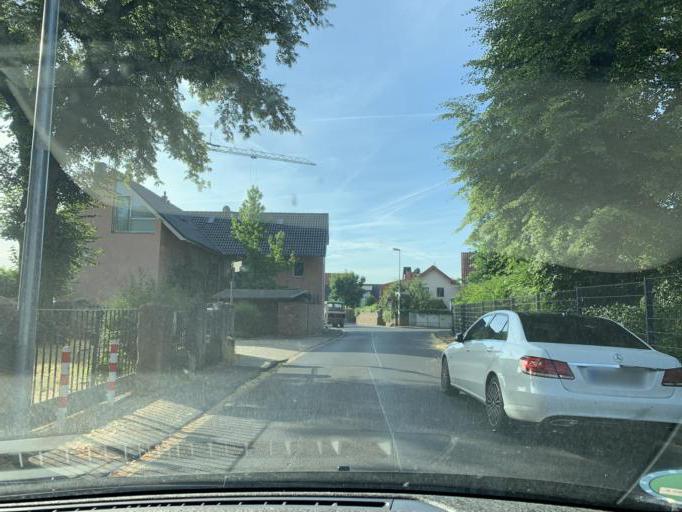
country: DE
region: North Rhine-Westphalia
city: Bornheim
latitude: 50.7858
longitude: 6.9504
